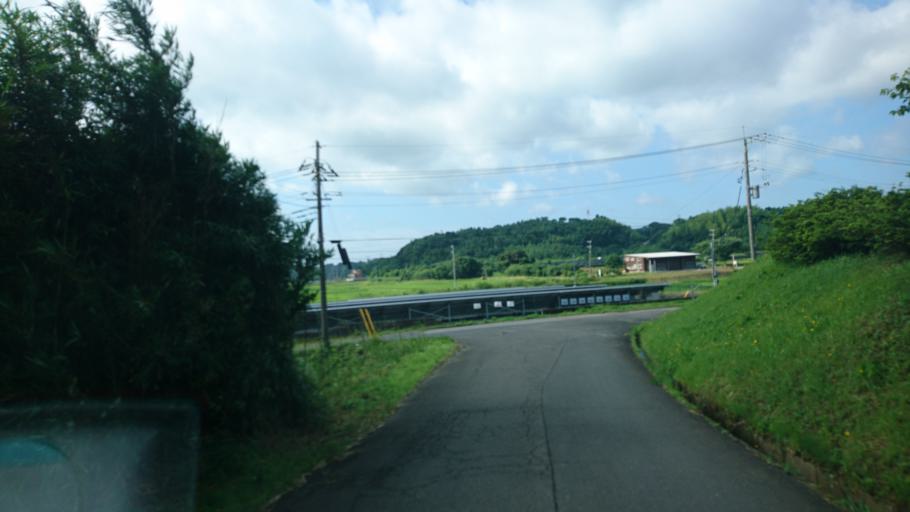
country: JP
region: Chiba
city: Sawara
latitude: 35.8716
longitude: 140.4792
